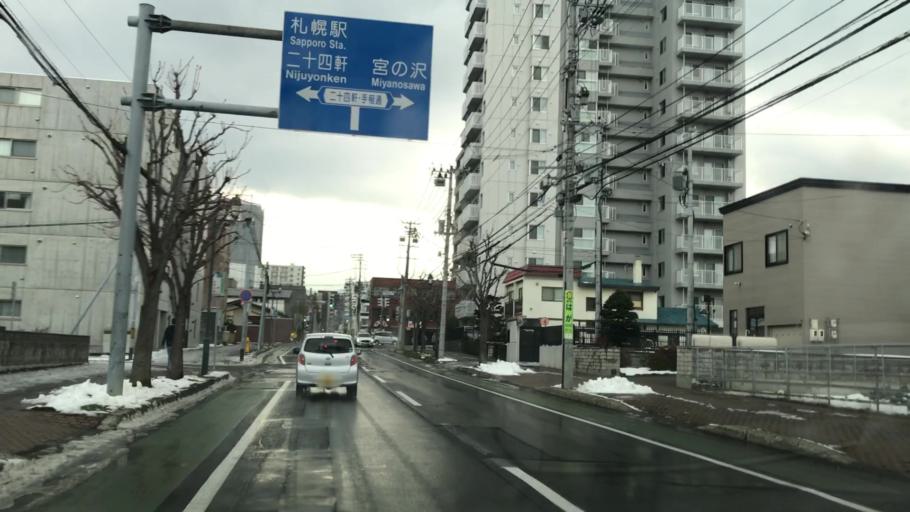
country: JP
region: Hokkaido
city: Sapporo
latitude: 43.0780
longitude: 141.3020
